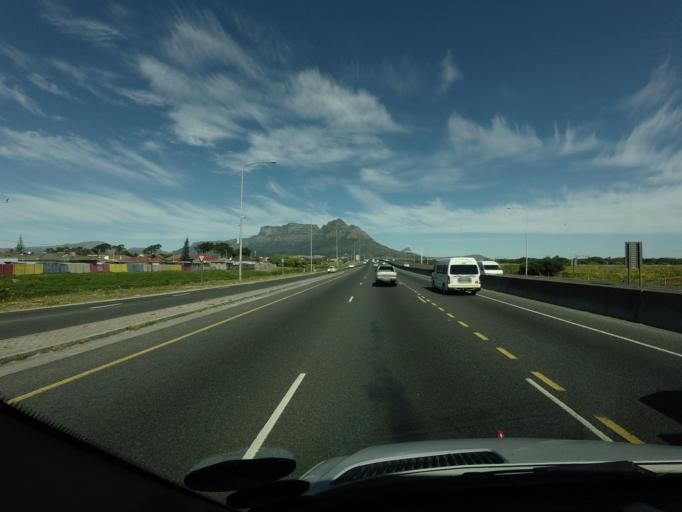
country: ZA
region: Western Cape
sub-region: City of Cape Town
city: Rosebank
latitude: -33.9499
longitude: 18.5076
